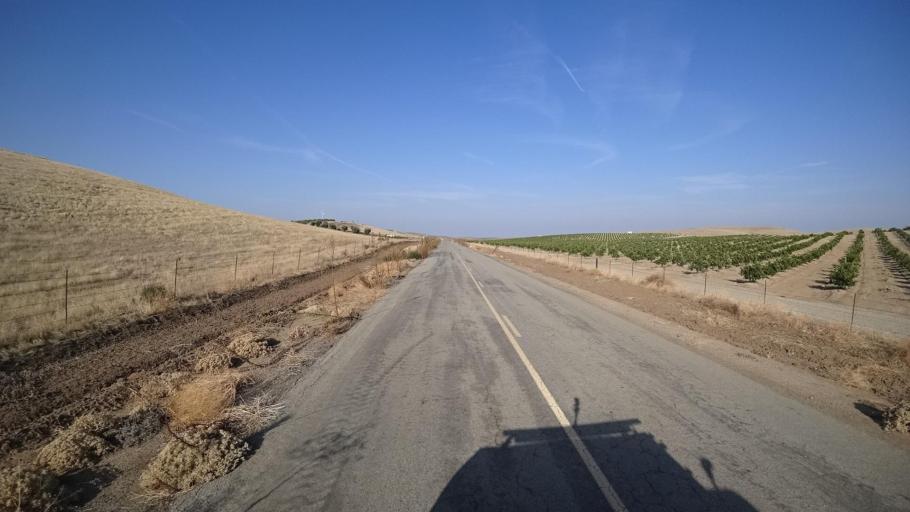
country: US
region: California
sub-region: Tulare County
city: Richgrove
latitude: 35.6425
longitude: -119.0484
